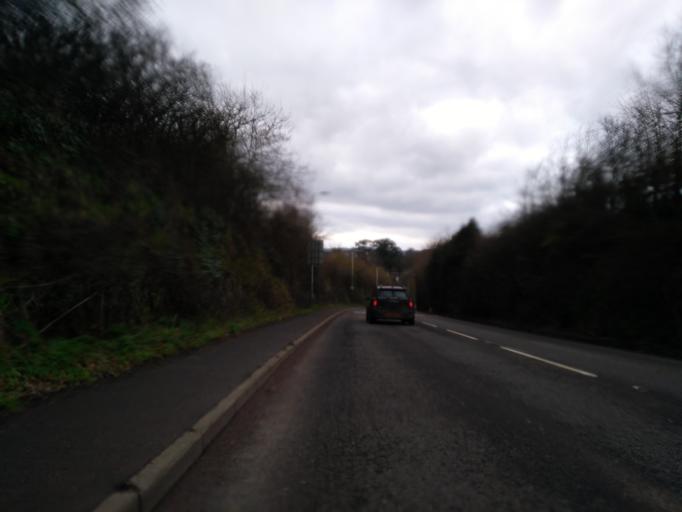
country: GB
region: England
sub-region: Devon
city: Crediton
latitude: 50.7693
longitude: -3.5847
